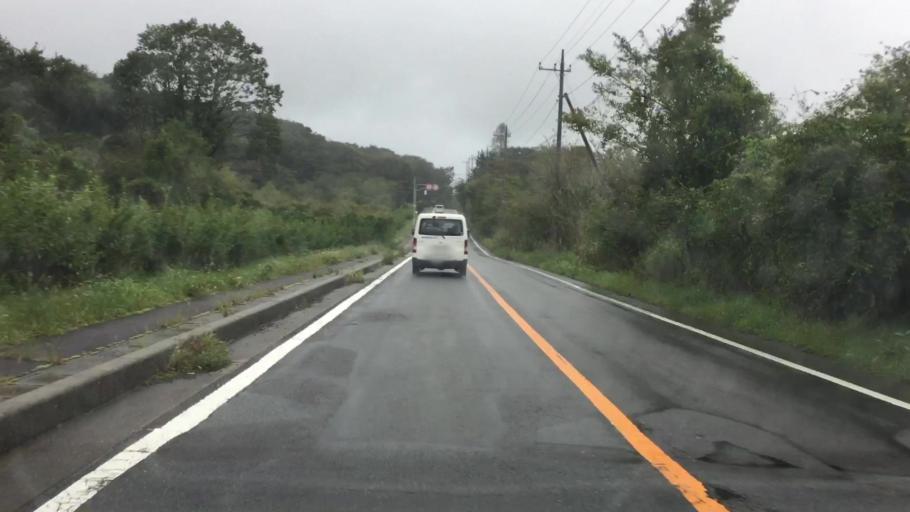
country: JP
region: Yamanashi
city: Fujikawaguchiko
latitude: 35.4269
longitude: 138.6280
